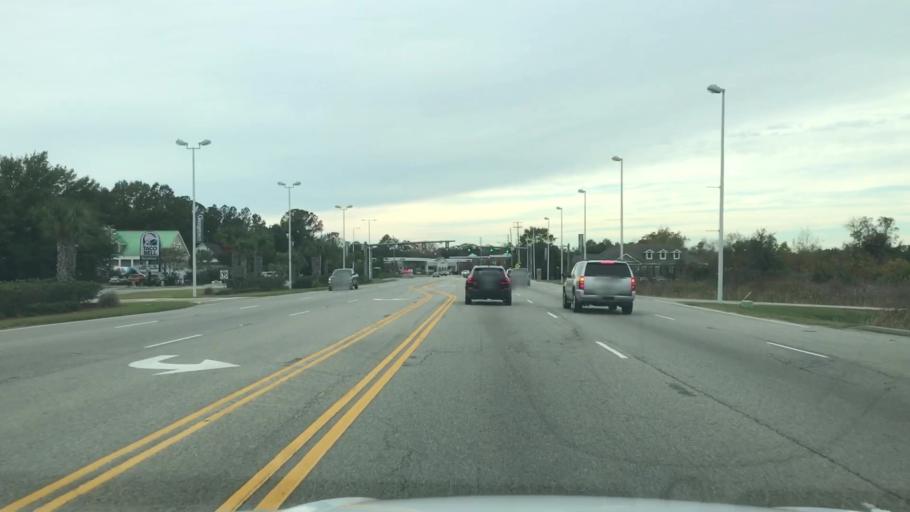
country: US
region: South Carolina
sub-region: Georgetown County
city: Georgetown
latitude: 33.3674
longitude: -79.2710
